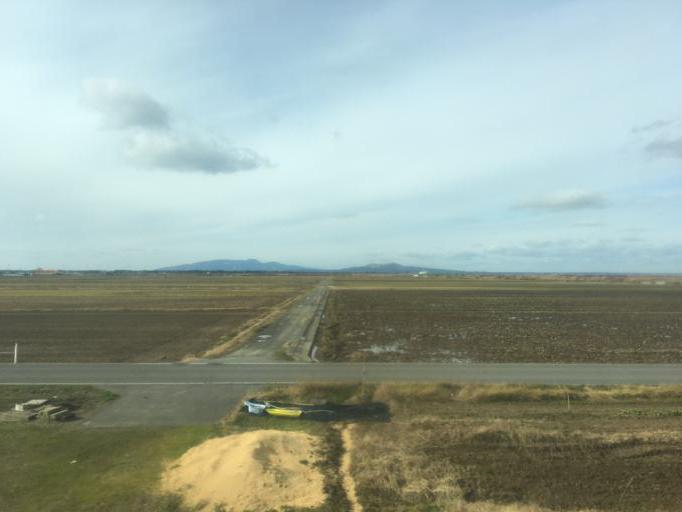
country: JP
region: Akita
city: Tenno
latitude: 39.8770
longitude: 140.0651
